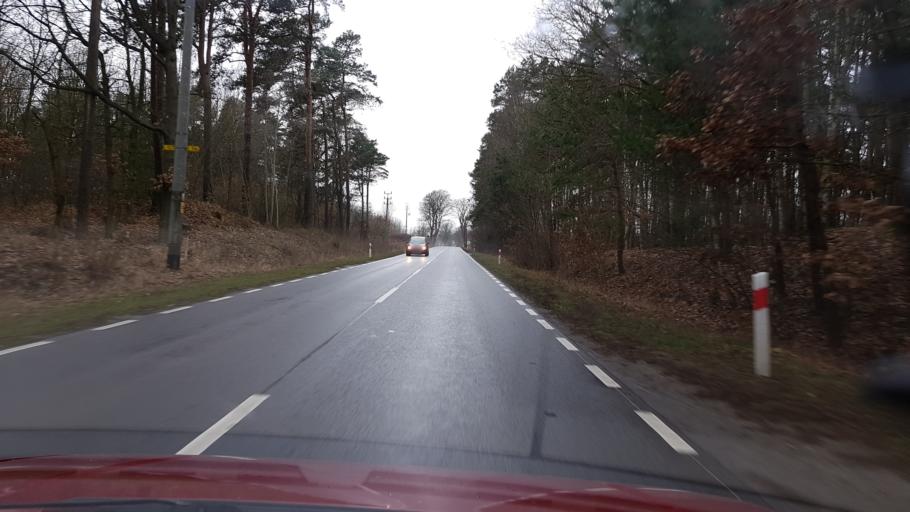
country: PL
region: West Pomeranian Voivodeship
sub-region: Powiat gryfinski
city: Gryfino
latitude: 53.2568
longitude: 14.5278
